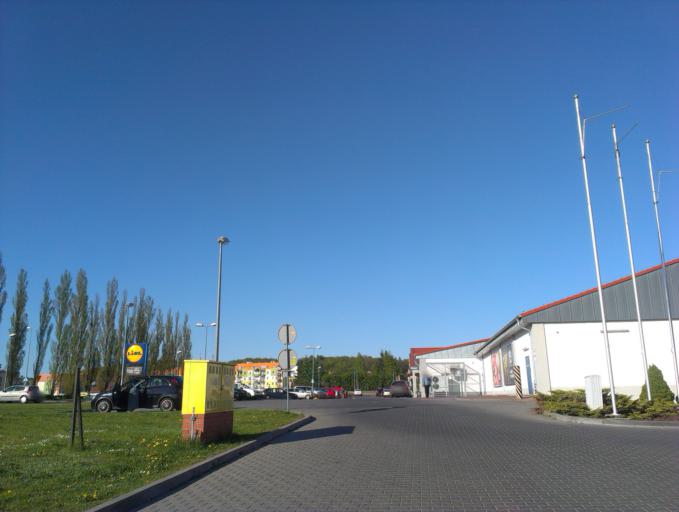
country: PL
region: West Pomeranian Voivodeship
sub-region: Koszalin
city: Koszalin
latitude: 54.2081
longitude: 16.2045
